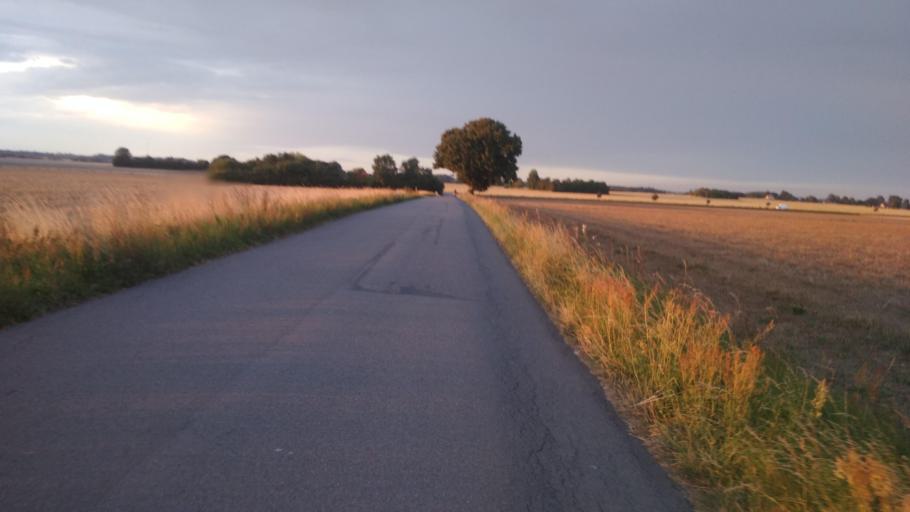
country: DK
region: Capital Region
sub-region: Bornholm Kommune
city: Akirkeby
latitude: 55.0318
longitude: 14.9138
